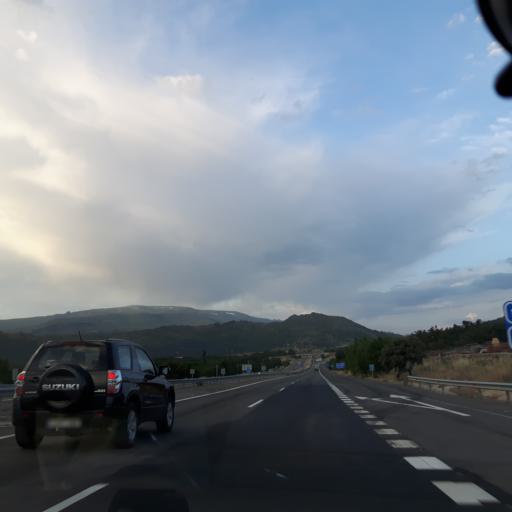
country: ES
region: Castille and Leon
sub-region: Provincia de Salamanca
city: Nava de Bejar
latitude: 40.4596
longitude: -5.6786
